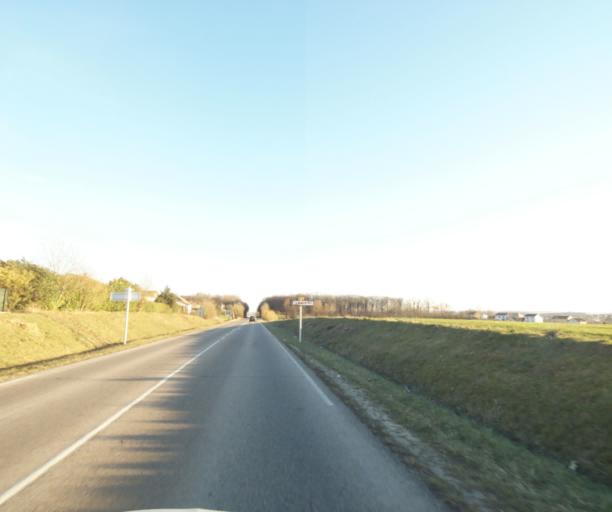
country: FR
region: Lorraine
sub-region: Departement de Meurthe-et-Moselle
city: Tomblaine
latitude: 48.6747
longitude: 6.2281
